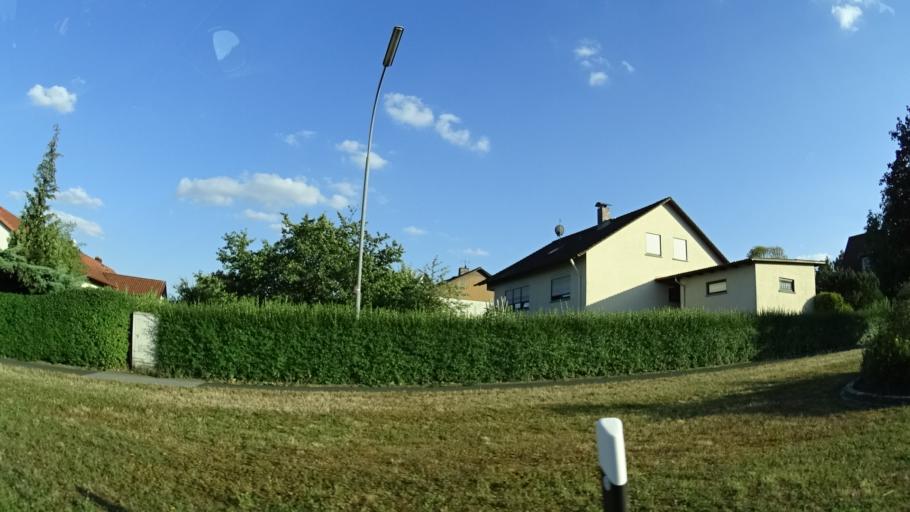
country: DE
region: Bavaria
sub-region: Regierungsbezirk Unterfranken
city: Mellrichstadt
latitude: 50.4288
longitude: 10.2948
